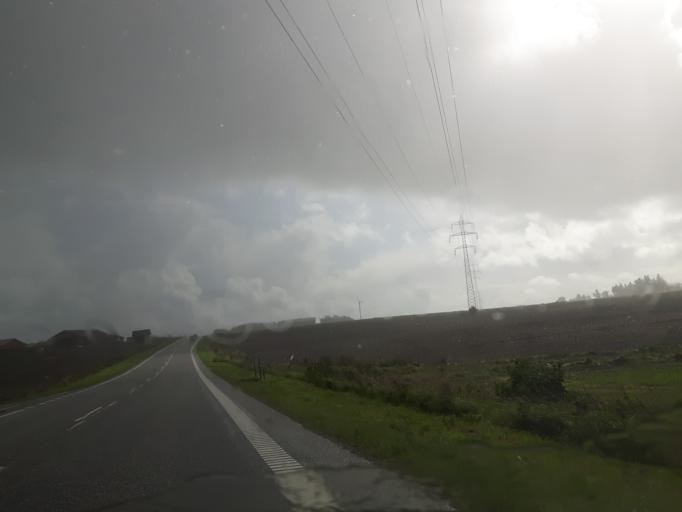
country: DK
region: Central Jutland
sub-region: Struer Kommune
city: Struer
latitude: 56.6228
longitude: 8.5182
